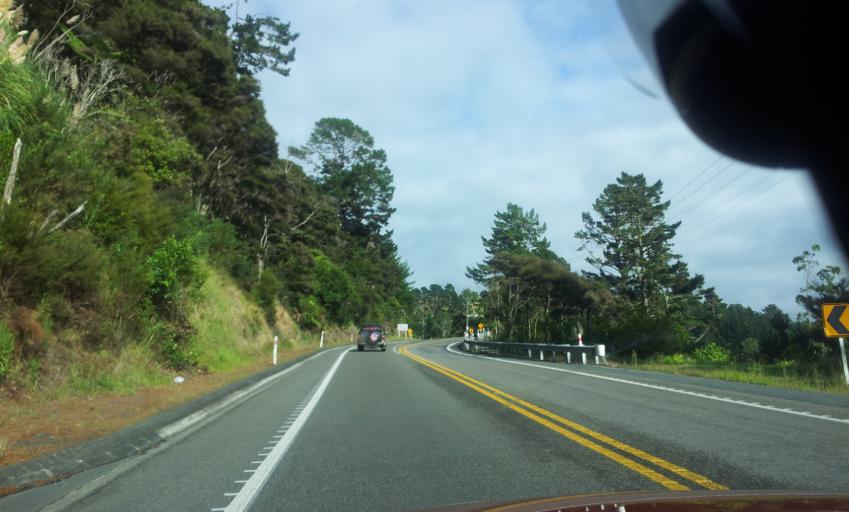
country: NZ
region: Auckland
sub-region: Auckland
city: Warkworth
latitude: -36.3679
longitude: 174.6205
